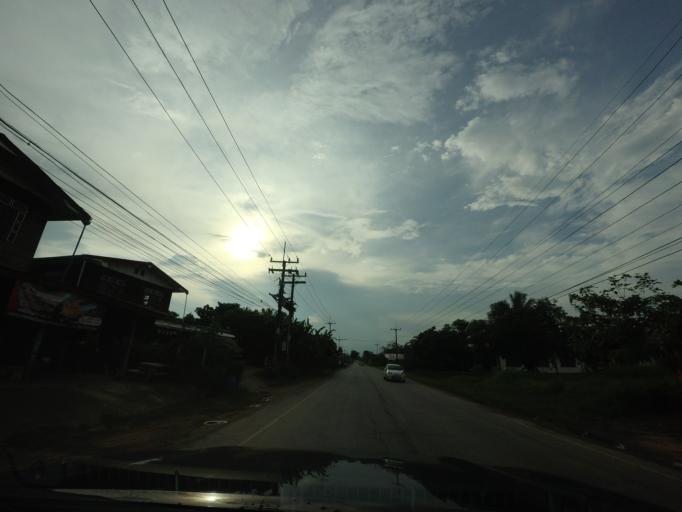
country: TH
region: Nong Khai
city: Pho Tak
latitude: 17.7795
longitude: 102.3901
